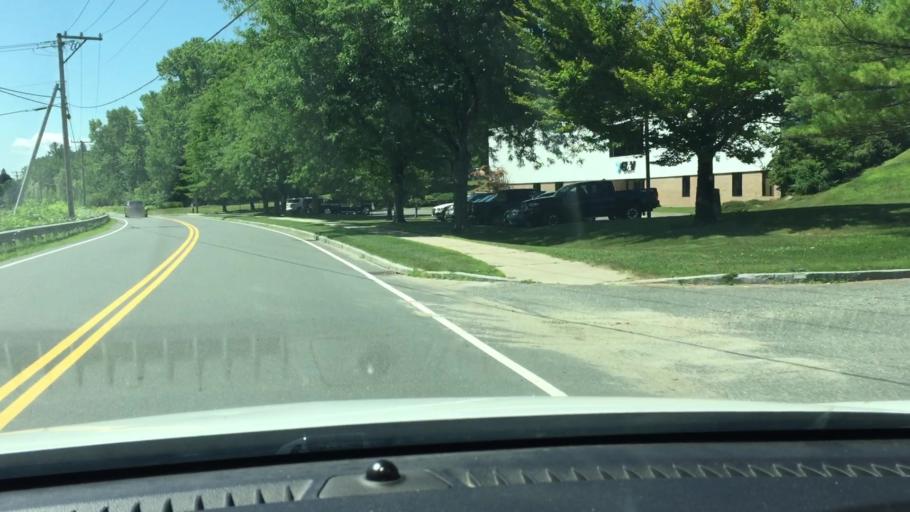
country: US
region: Massachusetts
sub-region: Berkshire County
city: Lenox
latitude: 42.3458
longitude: -73.2461
